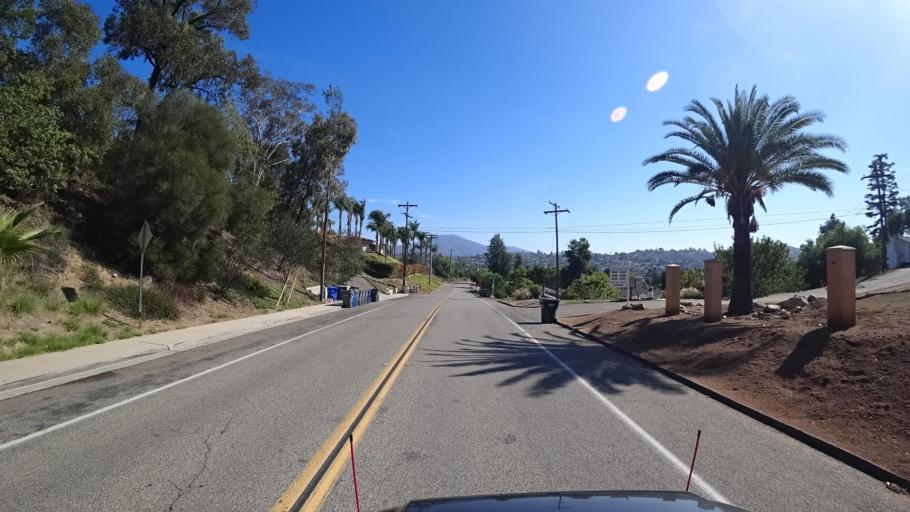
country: US
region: California
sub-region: San Diego County
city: Spring Valley
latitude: 32.7556
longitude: -116.9869
